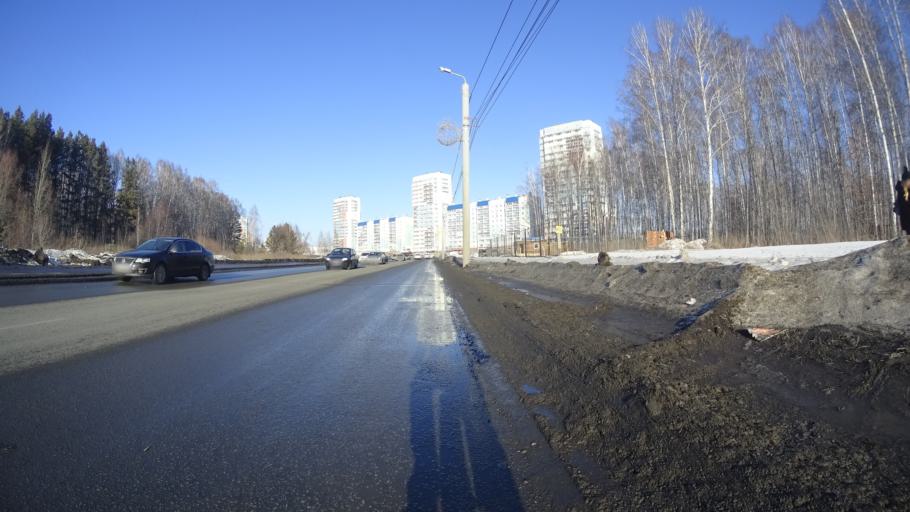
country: RU
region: Chelyabinsk
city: Roshchino
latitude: 55.2008
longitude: 61.2817
